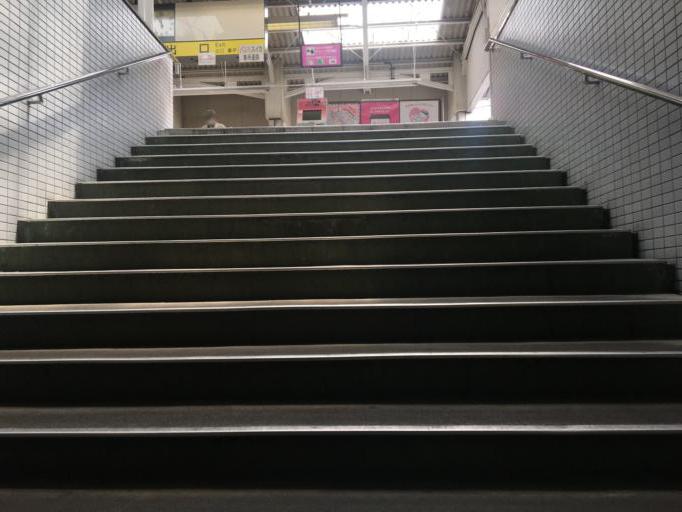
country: JP
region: Saitama
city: Kasukabe
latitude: 35.9642
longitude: 139.7663
